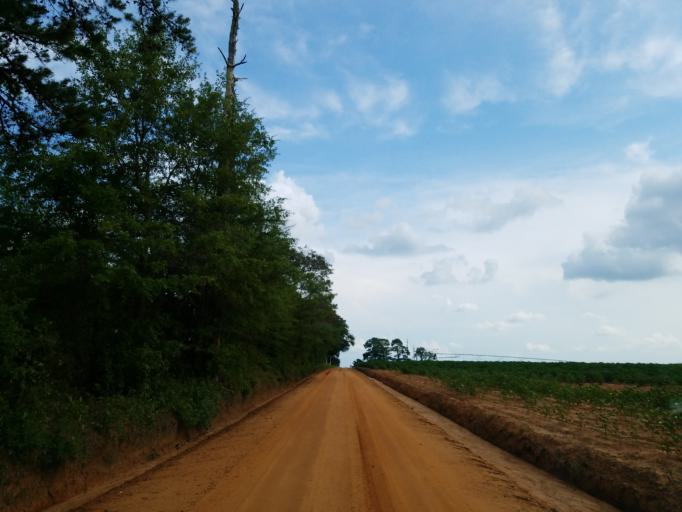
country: US
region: Georgia
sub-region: Dooly County
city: Unadilla
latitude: 32.2855
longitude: -83.7187
